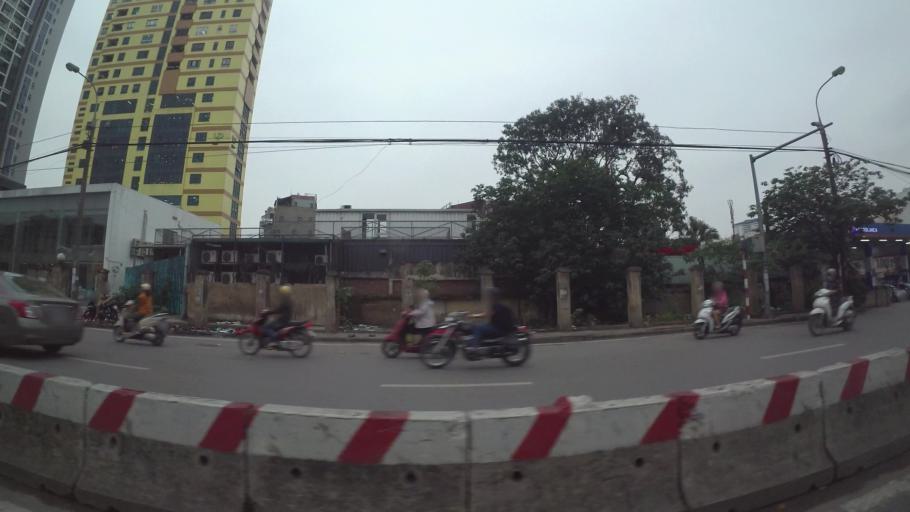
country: VN
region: Ha Noi
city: Hai BaTrung
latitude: 21.0127
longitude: 105.8635
